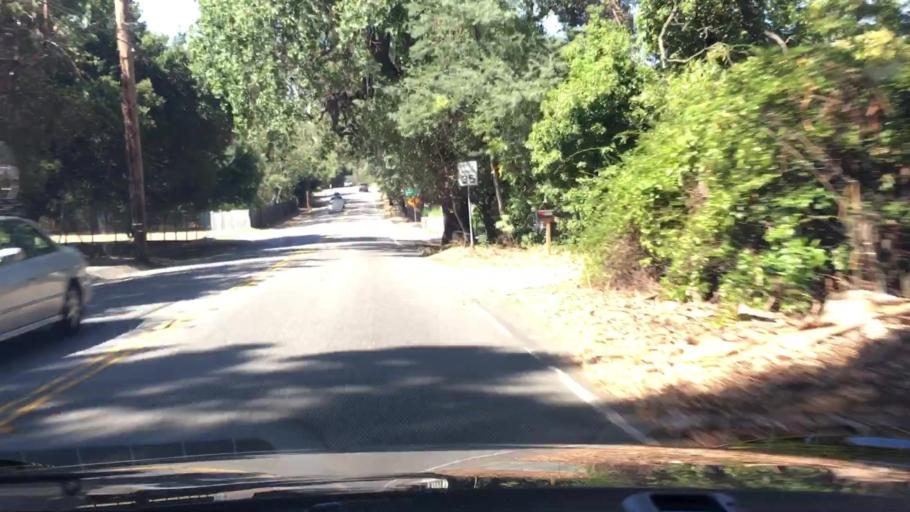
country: US
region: California
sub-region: Santa Clara County
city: Saratoga
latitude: 37.2465
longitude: -122.0138
